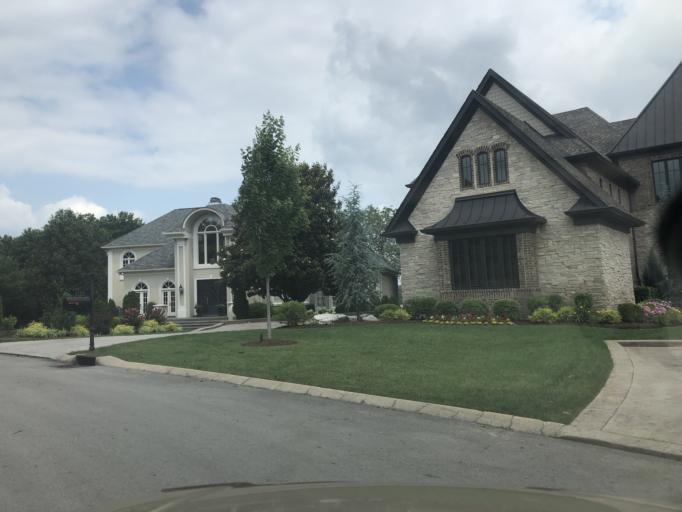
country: US
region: Tennessee
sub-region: Davidson County
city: Lakewood
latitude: 36.2410
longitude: -86.6031
